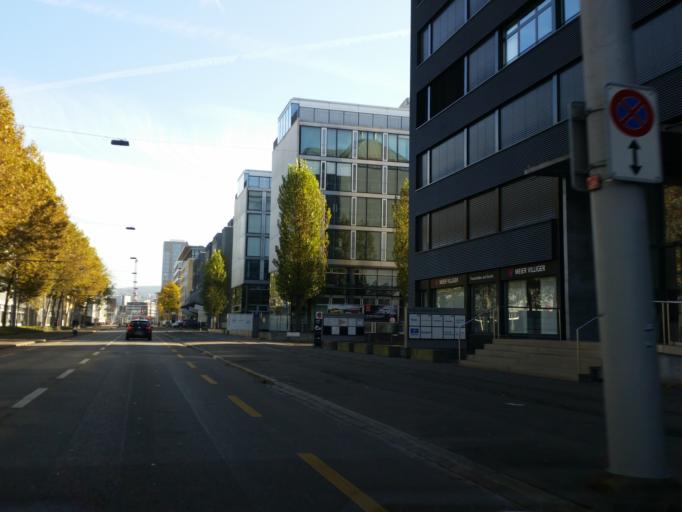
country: CH
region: Zurich
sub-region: Bezirk Zuerich
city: Zuerich (Kreis 5) / Escher-Wyss
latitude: 47.3933
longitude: 8.5134
